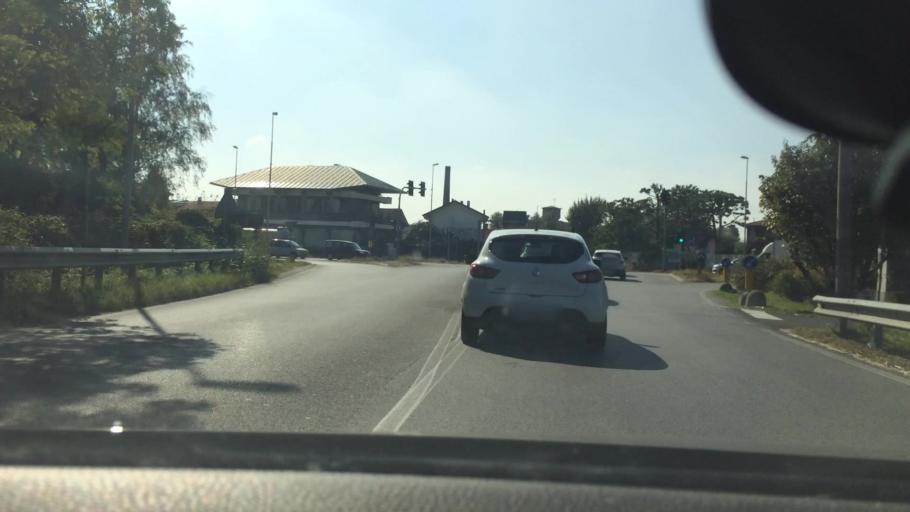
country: IT
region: Lombardy
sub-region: Citta metropolitana di Milano
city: Inveruno
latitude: 45.5206
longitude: 8.8581
